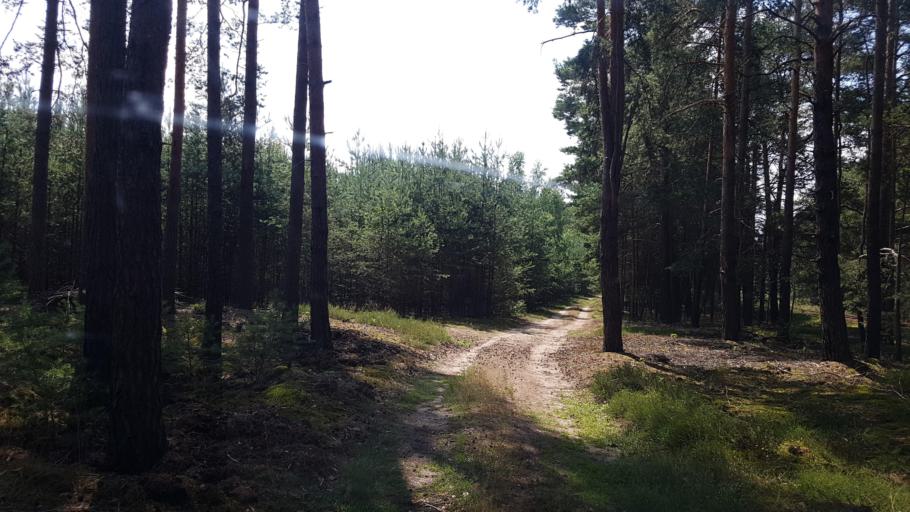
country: DE
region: Brandenburg
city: Crinitz
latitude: 51.6984
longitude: 13.7366
